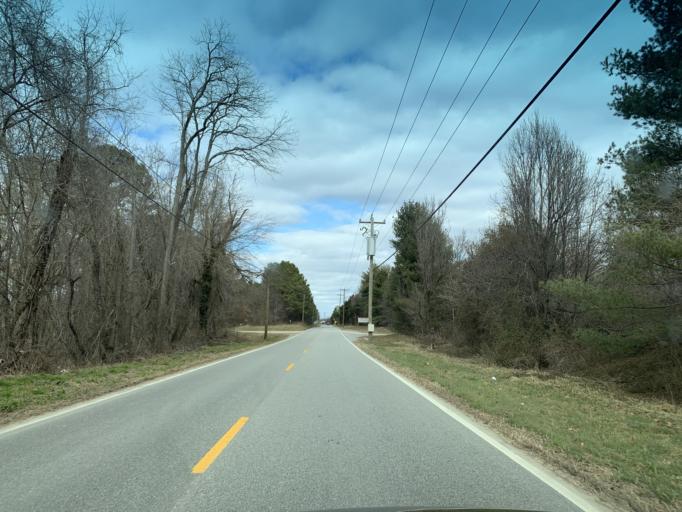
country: US
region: Maryland
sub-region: Queen Anne's County
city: Centreville
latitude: 39.0041
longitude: -76.1340
